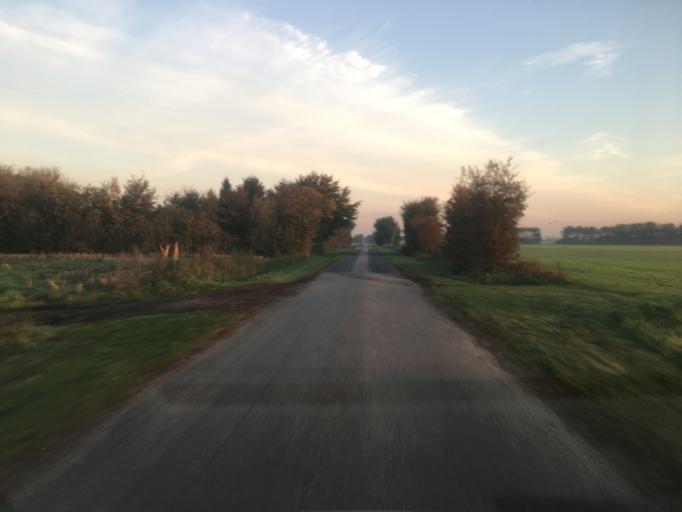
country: DK
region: South Denmark
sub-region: Tonder Kommune
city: Logumkloster
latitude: 55.0550
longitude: 9.0239
